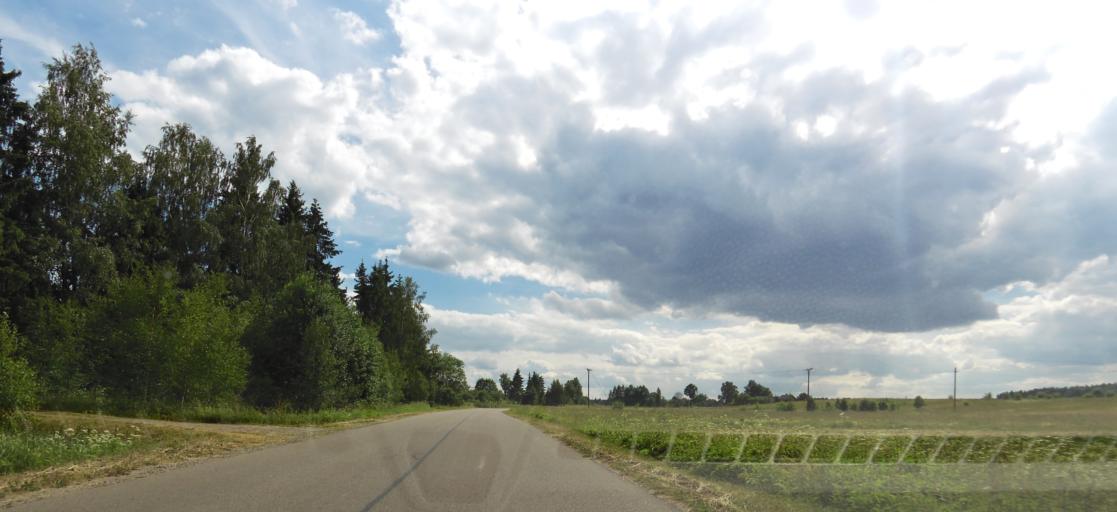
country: LT
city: Skaidiskes
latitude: 54.5368
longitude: 25.6451
